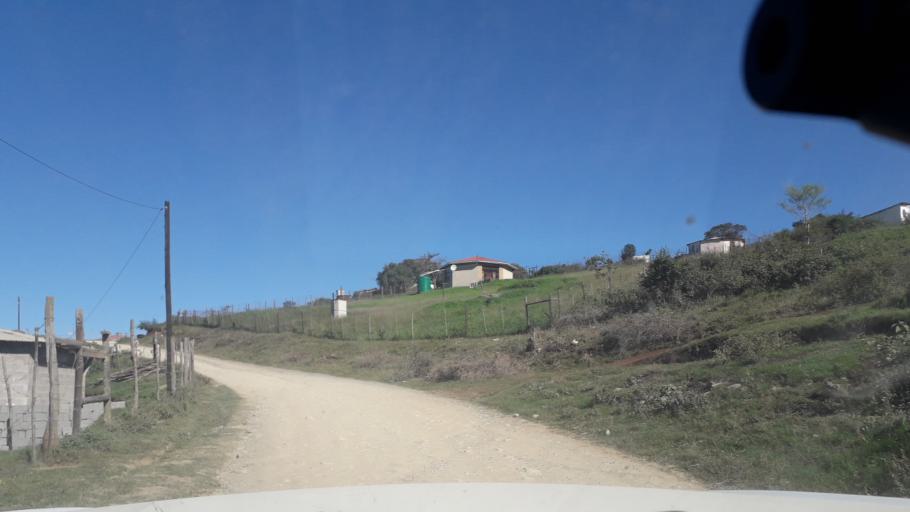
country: ZA
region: Eastern Cape
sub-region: Amathole District Municipality
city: Komga
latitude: -32.7661
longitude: 27.9482
